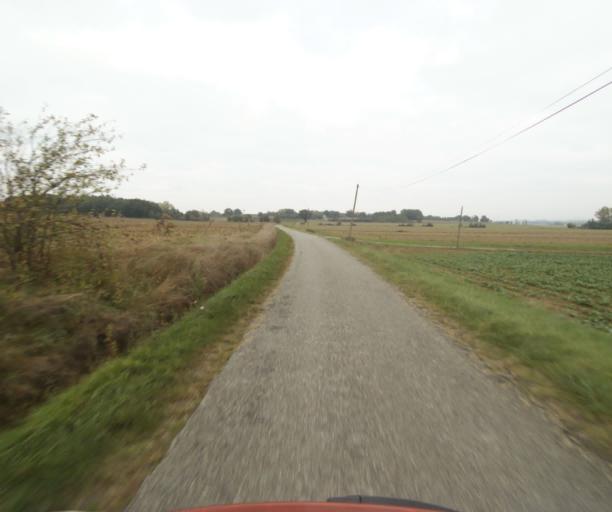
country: FR
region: Midi-Pyrenees
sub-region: Departement du Tarn-et-Garonne
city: Verdun-sur-Garonne
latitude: 43.8138
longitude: 1.2068
